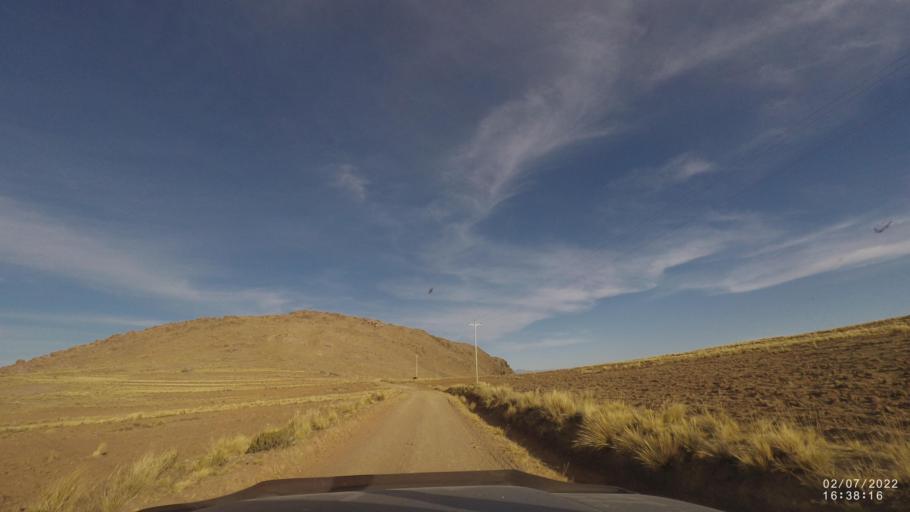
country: BO
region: Cochabamba
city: Irpa Irpa
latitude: -17.9694
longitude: -66.4968
